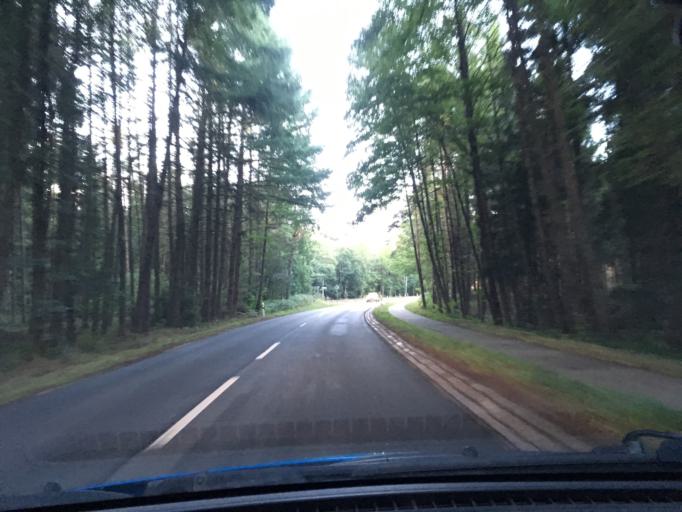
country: DE
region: Lower Saxony
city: Fassberg
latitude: 52.8841
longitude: 10.1421
